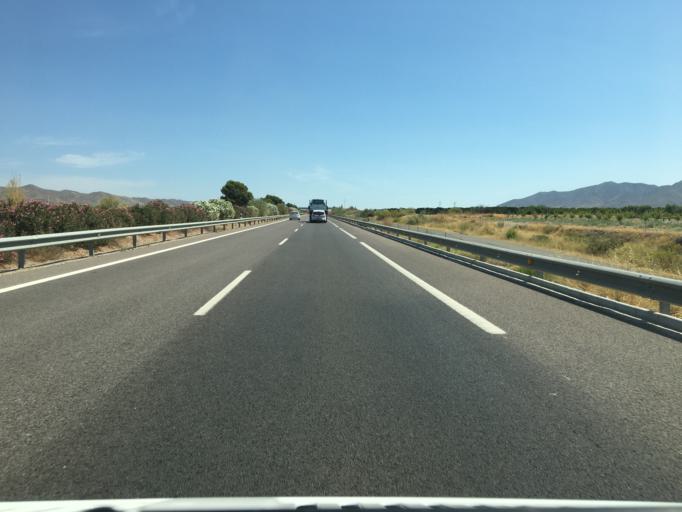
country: ES
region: Andalusia
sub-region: Provincia de Almeria
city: Huercal-Overa
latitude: 37.4501
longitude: -1.8961
